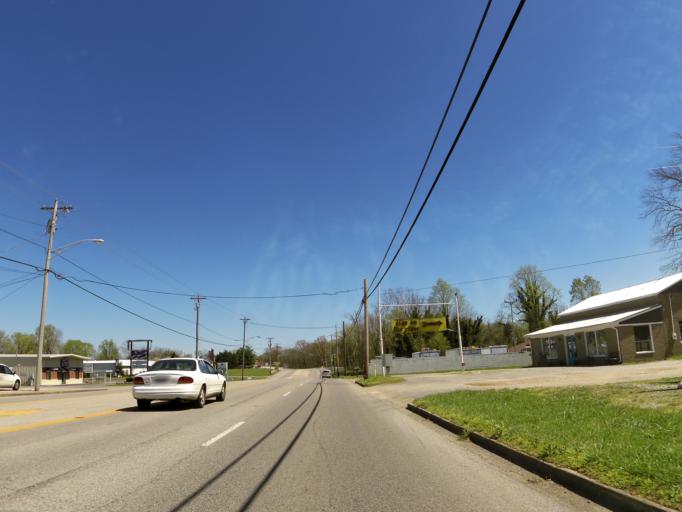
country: US
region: Kentucky
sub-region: Warren County
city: Bowling Green
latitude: 37.0061
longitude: -86.4148
